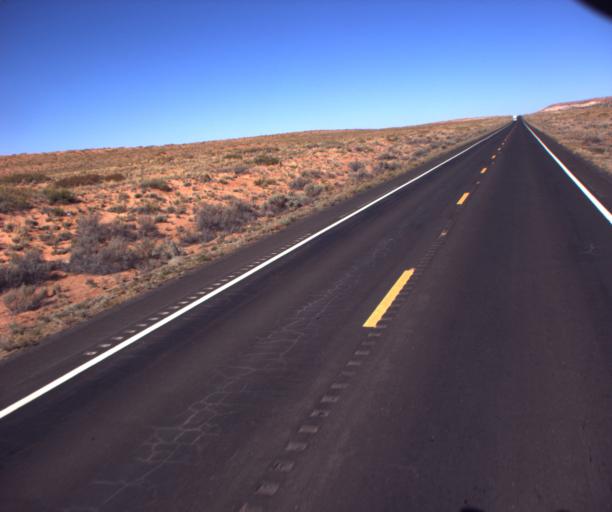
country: US
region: Arizona
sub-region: Coconino County
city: Tuba City
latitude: 36.2120
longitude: -111.0485
